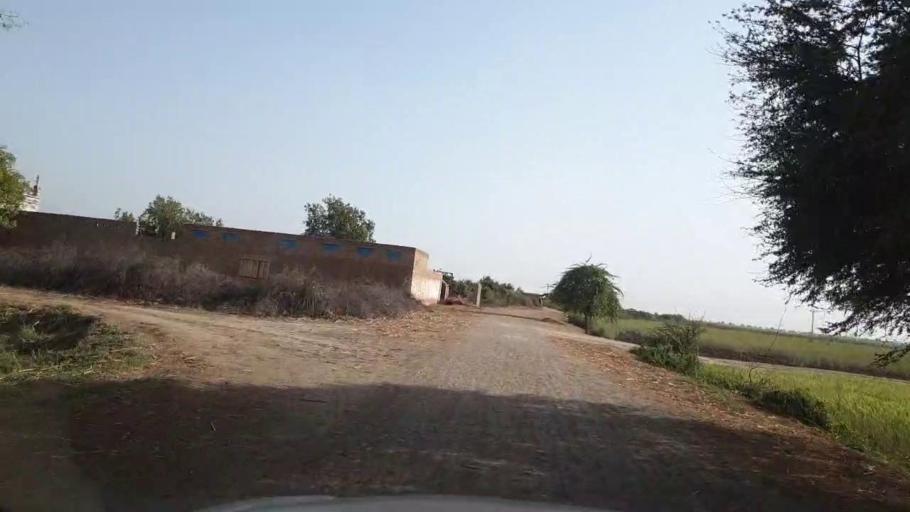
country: PK
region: Sindh
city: Tando Ghulam Ali
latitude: 25.0694
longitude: 68.8917
